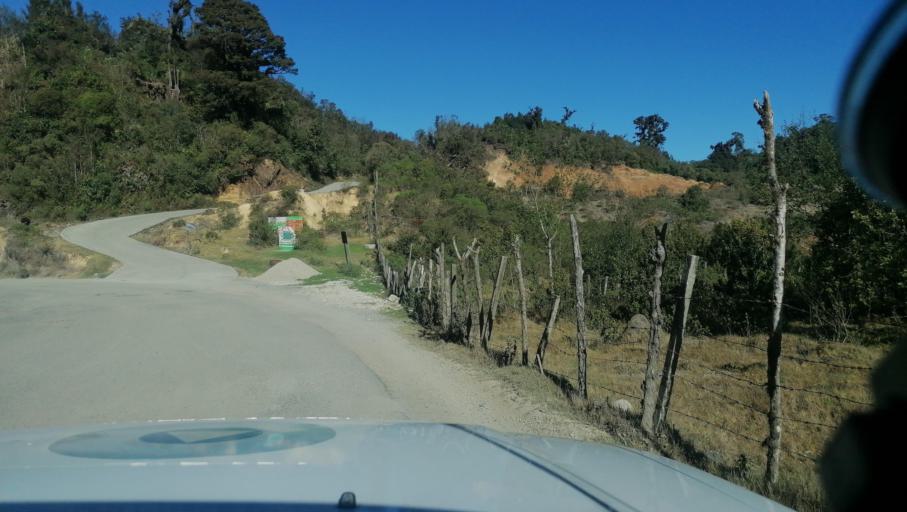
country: MX
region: Chiapas
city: Motozintla de Mendoza
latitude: 15.2661
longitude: -92.2212
